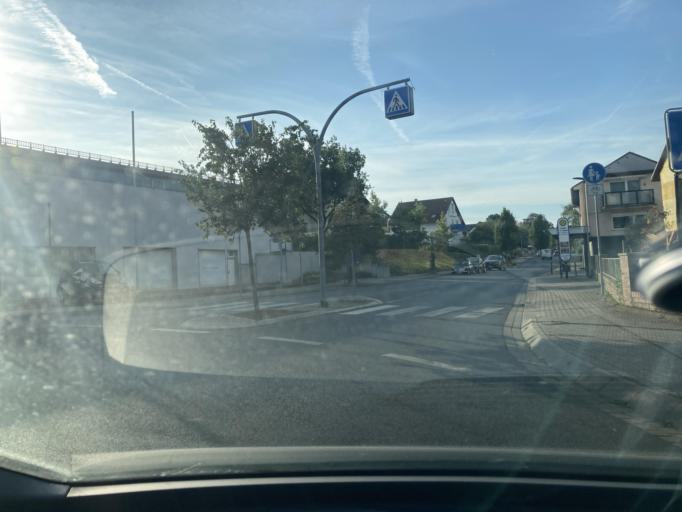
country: DE
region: Hesse
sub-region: Regierungsbezirk Darmstadt
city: Bad Vilbel
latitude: 50.1926
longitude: 8.7232
